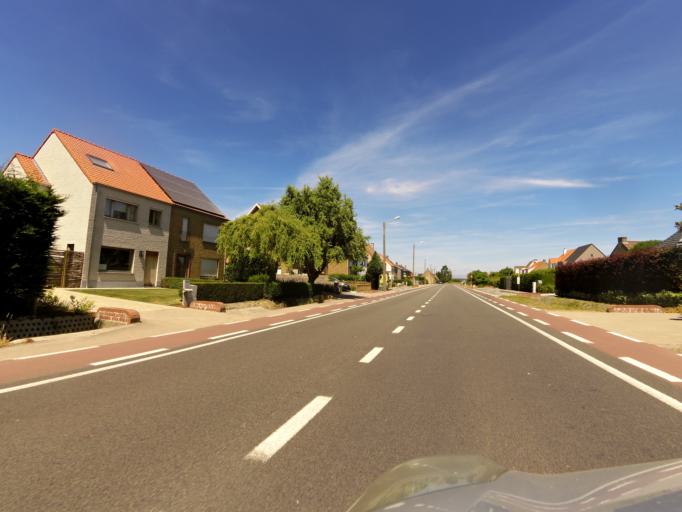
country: BE
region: Flanders
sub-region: Provincie West-Vlaanderen
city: Damme
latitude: 51.2805
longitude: 3.2332
